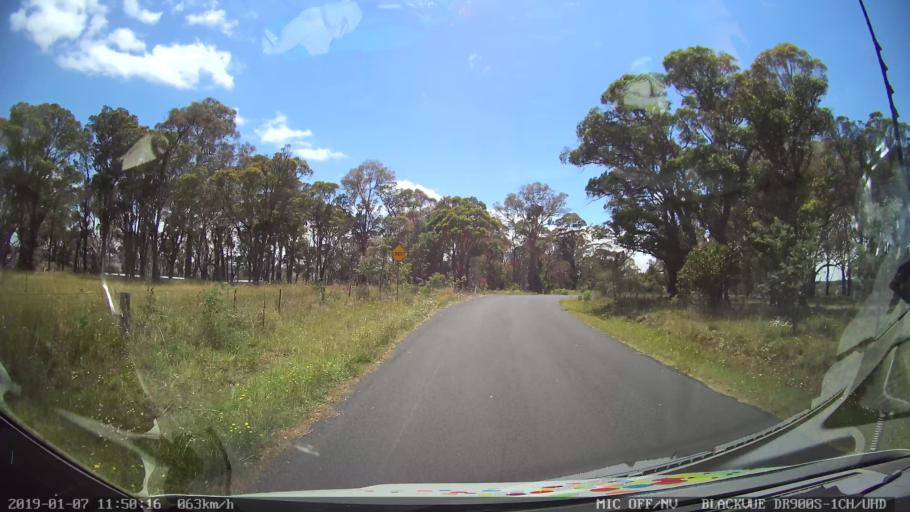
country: AU
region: New South Wales
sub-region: Guyra
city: Guyra
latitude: -30.3129
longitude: 151.6342
